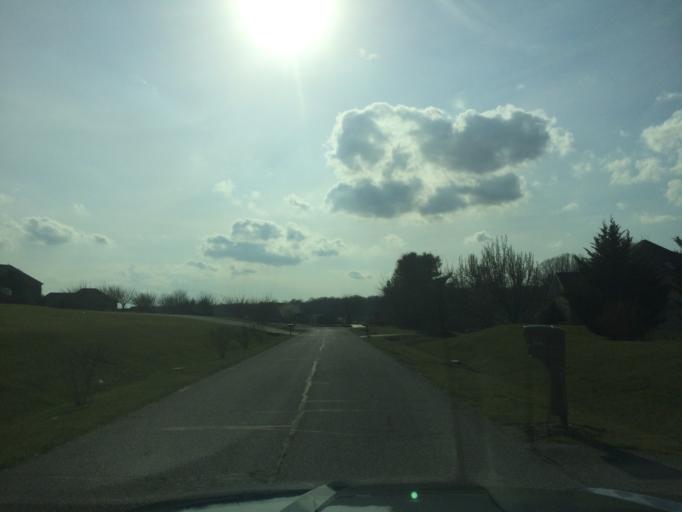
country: US
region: Maryland
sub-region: Howard County
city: Highland
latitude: 39.2076
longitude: -76.9489
